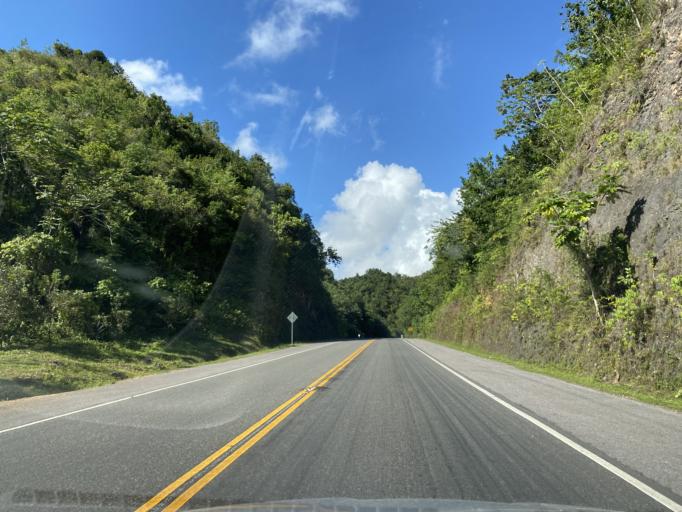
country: DO
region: Monte Plata
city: Majagual
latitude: 19.0715
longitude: -69.8293
